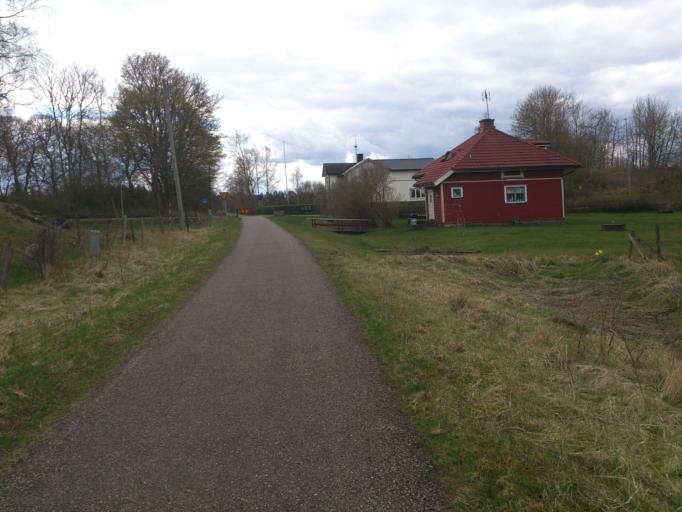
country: SE
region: Vaestra Goetaland
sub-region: Falkopings Kommun
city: Falkoeping
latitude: 57.9817
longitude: 13.5244
